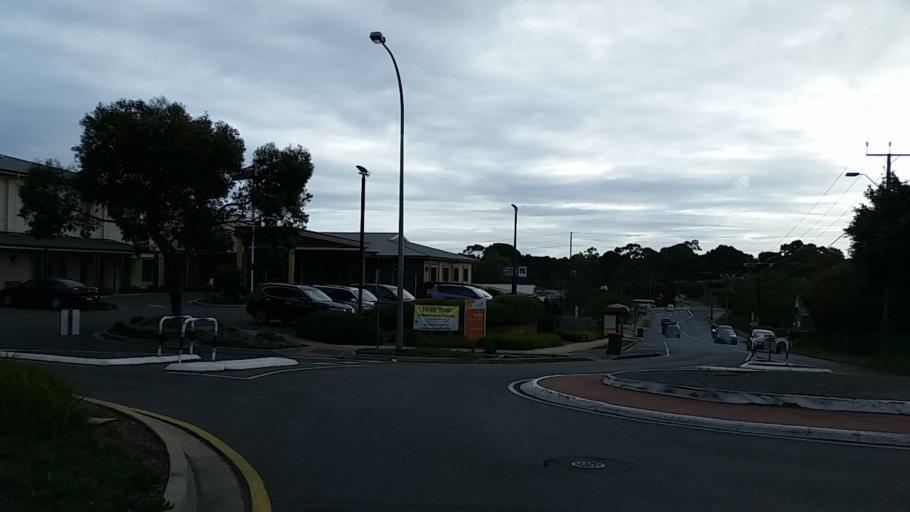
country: AU
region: South Australia
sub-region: Onkaparinga
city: Hackham
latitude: -35.1471
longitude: 138.5277
